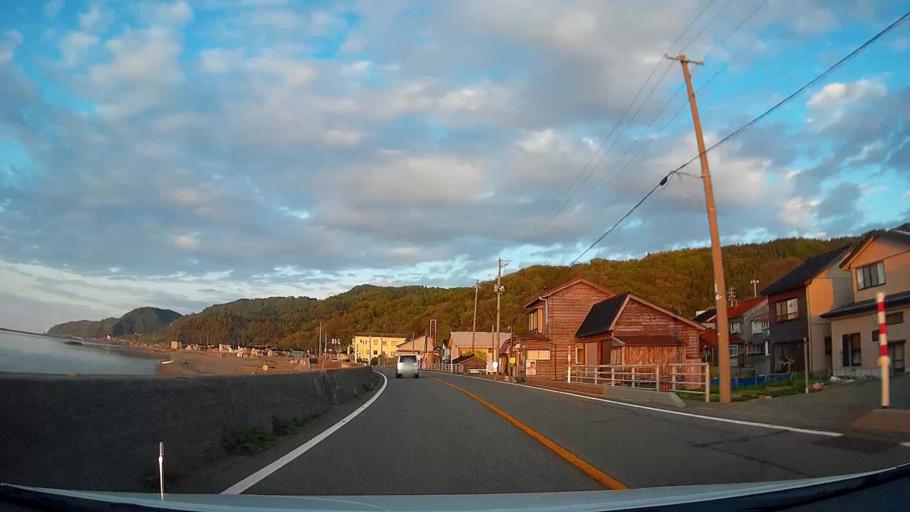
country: JP
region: Niigata
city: Joetsu
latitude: 37.1207
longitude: 138.0348
